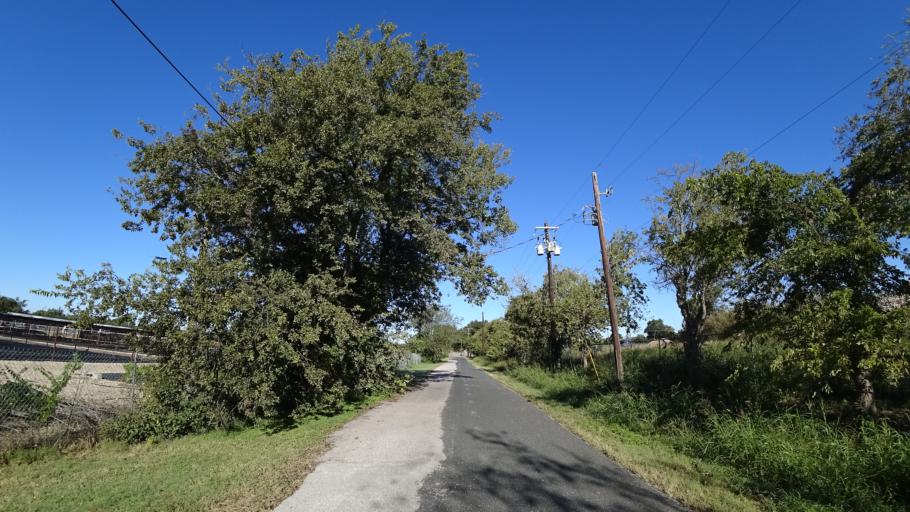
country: US
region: Texas
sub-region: Travis County
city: Austin
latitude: 30.2290
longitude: -97.6698
